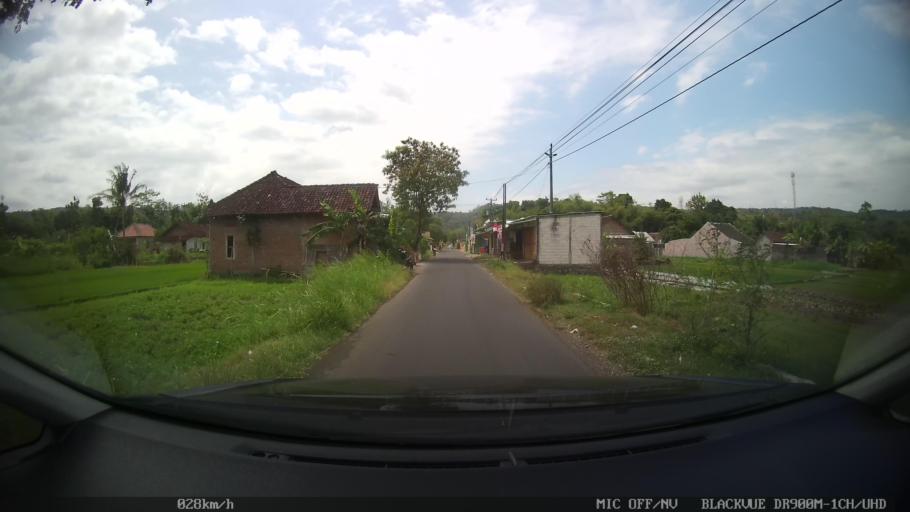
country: ID
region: Central Java
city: Candi Prambanan
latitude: -7.8141
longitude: 110.4956
